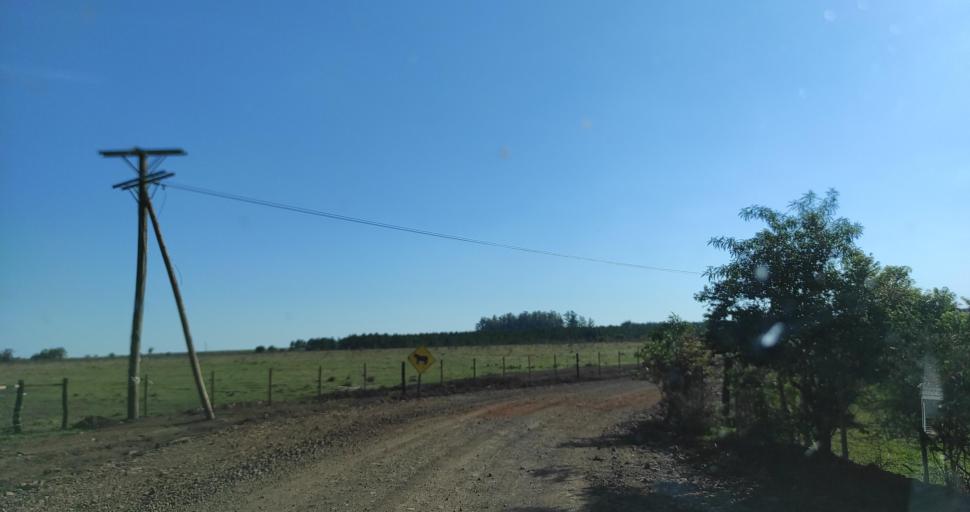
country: PY
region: Itapua
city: San Juan del Parana
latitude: -27.4255
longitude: -56.0960
